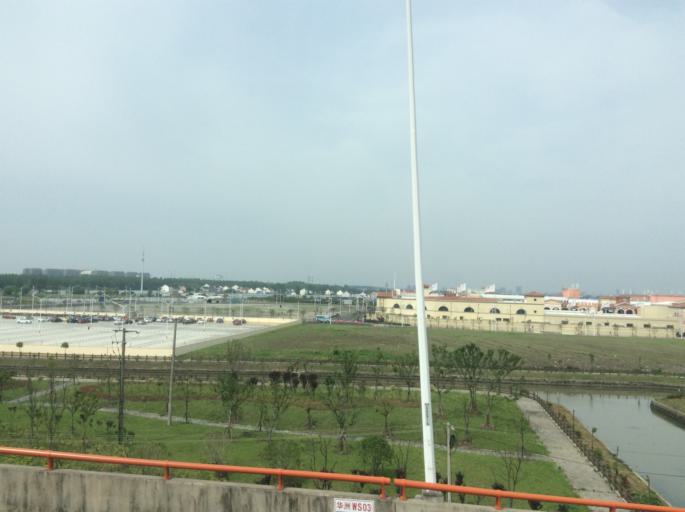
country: CN
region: Shanghai Shi
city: Laogang
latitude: 31.1983
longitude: 121.7639
